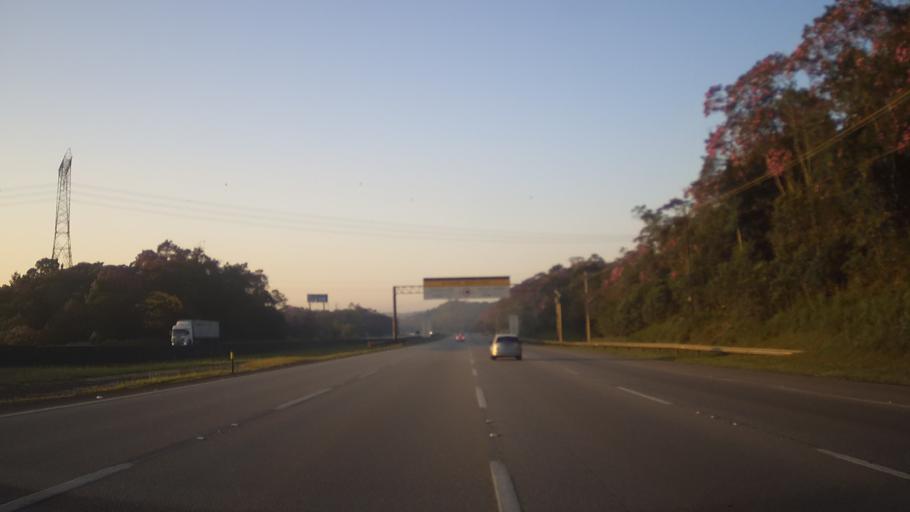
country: BR
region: Sao Paulo
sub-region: Cubatao
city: Cubatao
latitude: -23.8581
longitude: -46.5741
